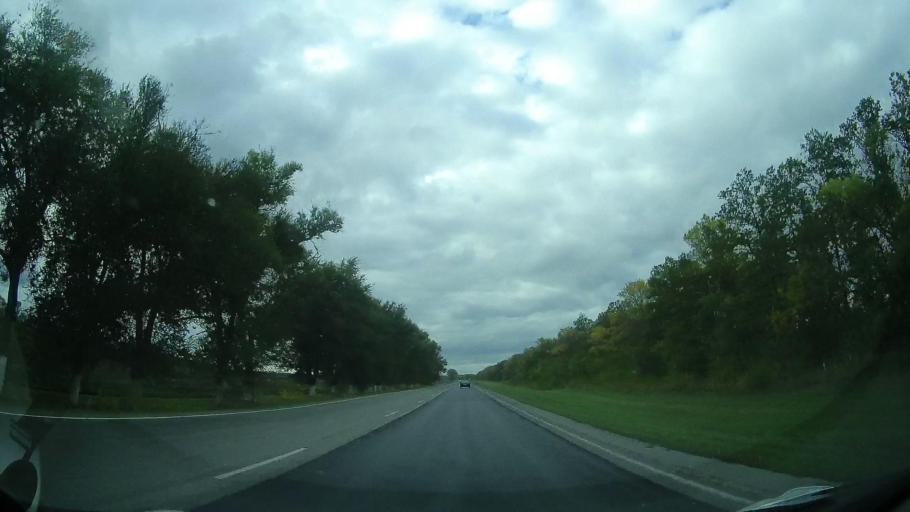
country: RU
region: Rostov
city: Zernograd
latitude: 46.7985
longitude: 40.3682
